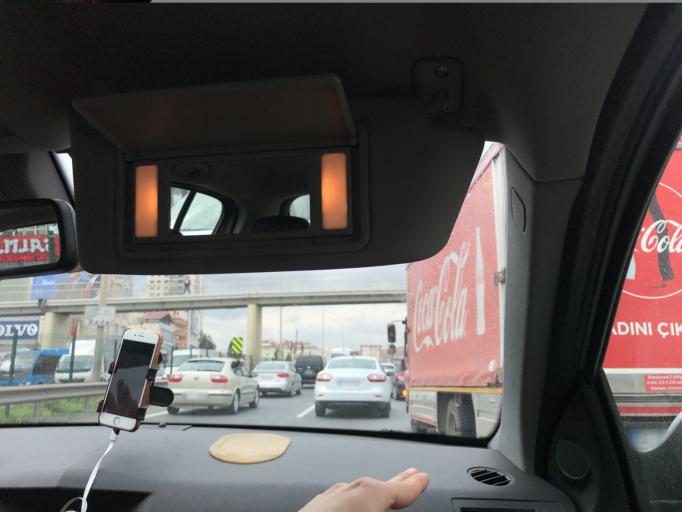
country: TR
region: Istanbul
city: Pendik
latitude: 40.8709
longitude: 29.2687
